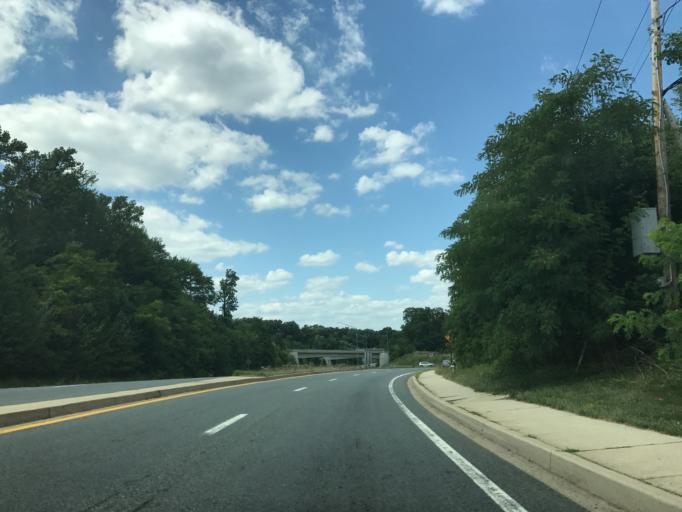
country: US
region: Maryland
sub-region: Prince George's County
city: South Laurel
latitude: 39.0531
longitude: -76.8373
